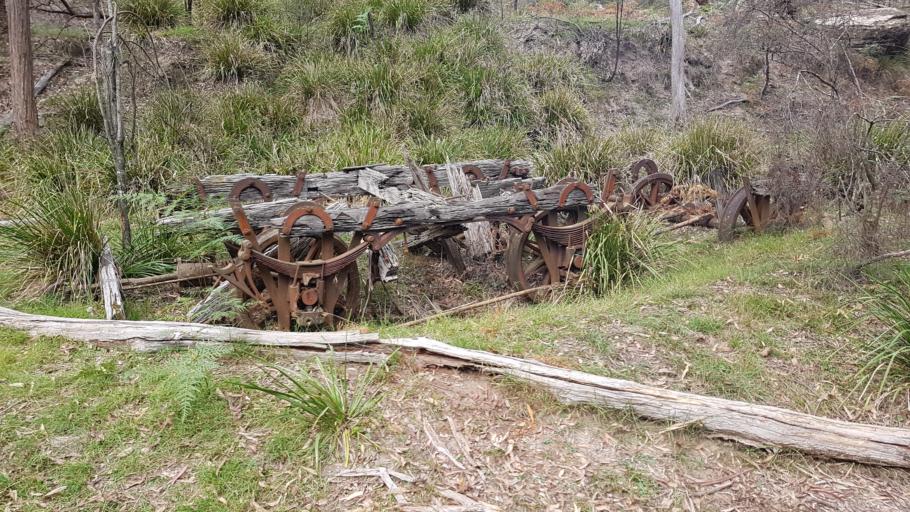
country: AU
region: New South Wales
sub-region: Lithgow
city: Lithgow
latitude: -33.2008
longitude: 150.2455
